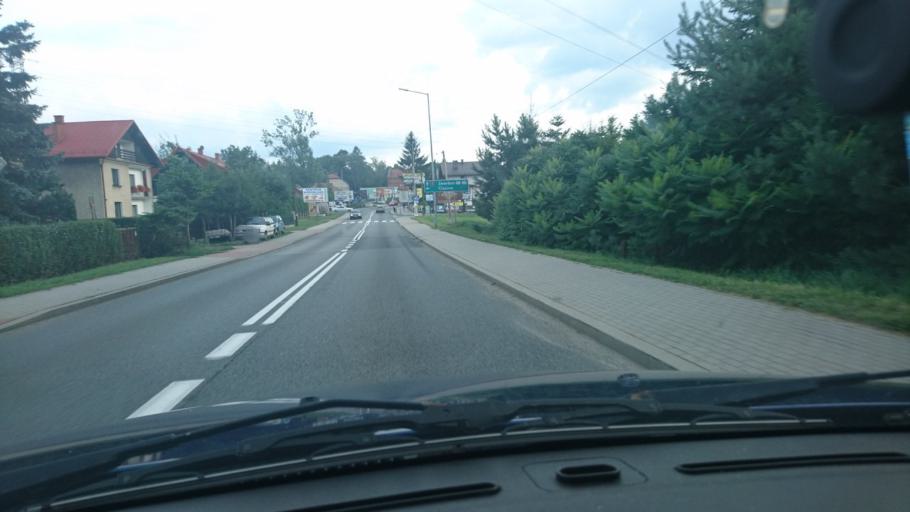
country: PL
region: Silesian Voivodeship
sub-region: Powiat zywiecki
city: Wegierska Gorka
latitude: 49.6078
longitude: 19.1162
